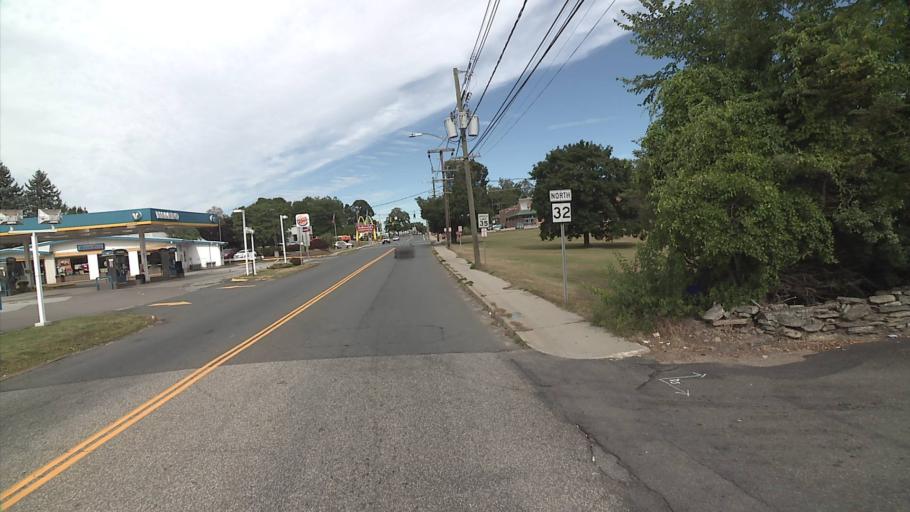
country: US
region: Connecticut
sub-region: Windham County
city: Willimantic
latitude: 41.7166
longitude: -72.2323
